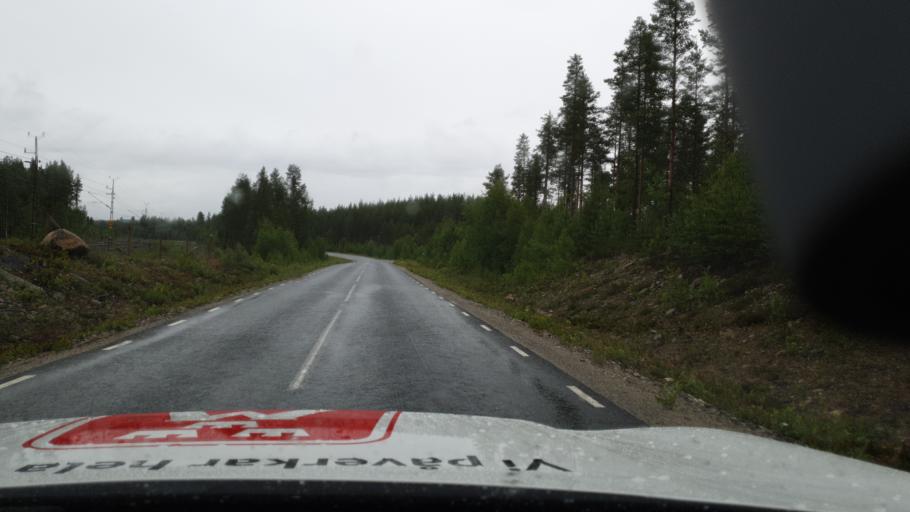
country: SE
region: Vaesterbotten
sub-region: Vindelns Kommun
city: Vindeln
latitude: 64.4430
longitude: 19.7488
